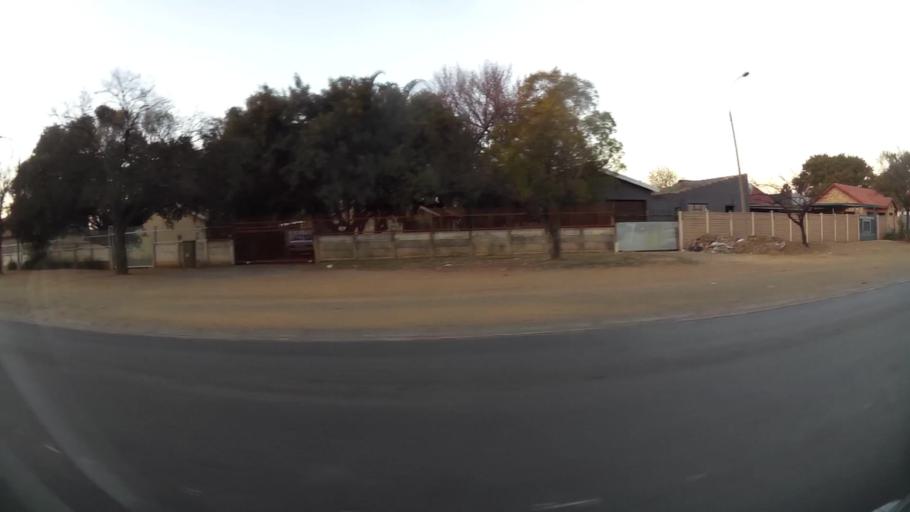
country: ZA
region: North-West
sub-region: Bojanala Platinum District Municipality
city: Rustenburg
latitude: -25.6565
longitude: 27.2445
